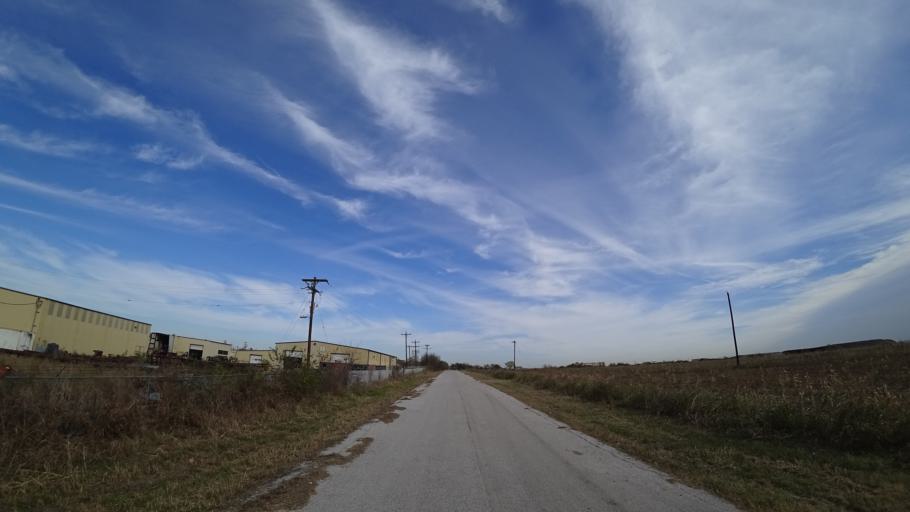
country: US
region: Texas
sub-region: Travis County
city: Onion Creek
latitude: 30.1540
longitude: -97.6946
